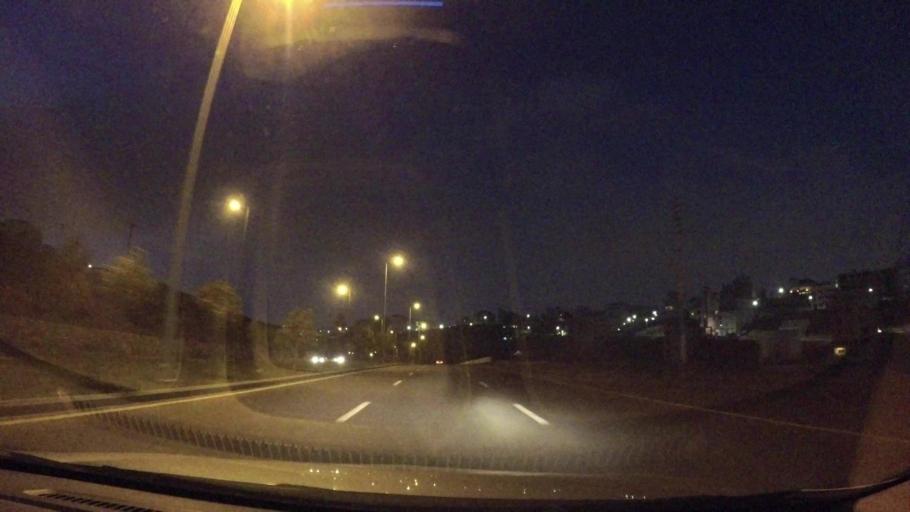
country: JO
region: Amman
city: Al Bunayyat ash Shamaliyah
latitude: 31.9166
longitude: 35.8796
